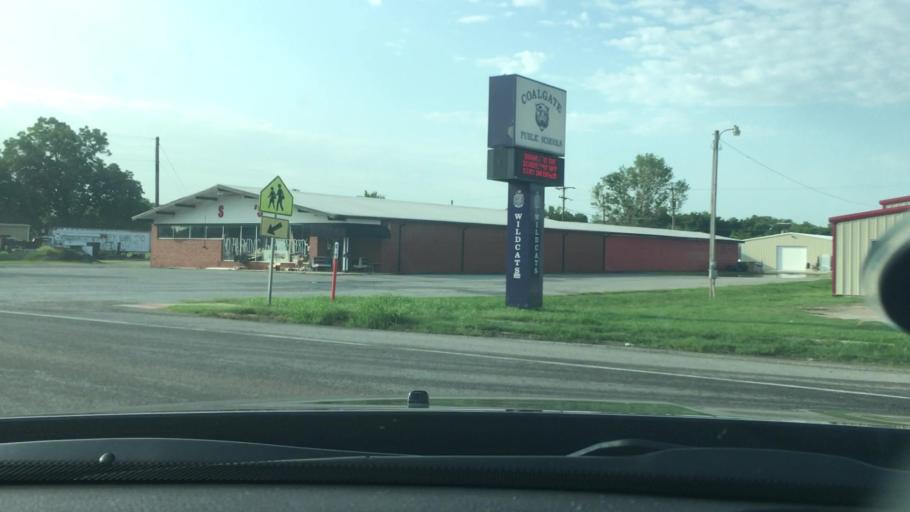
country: US
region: Oklahoma
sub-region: Coal County
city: Coalgate
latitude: 34.5366
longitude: -96.2181
